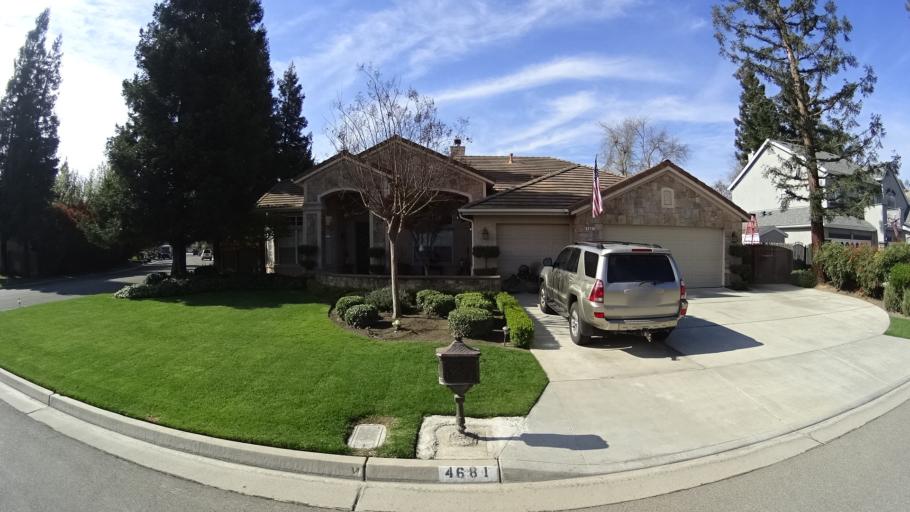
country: US
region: California
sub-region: Fresno County
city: West Park
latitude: 36.8434
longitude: -119.8767
